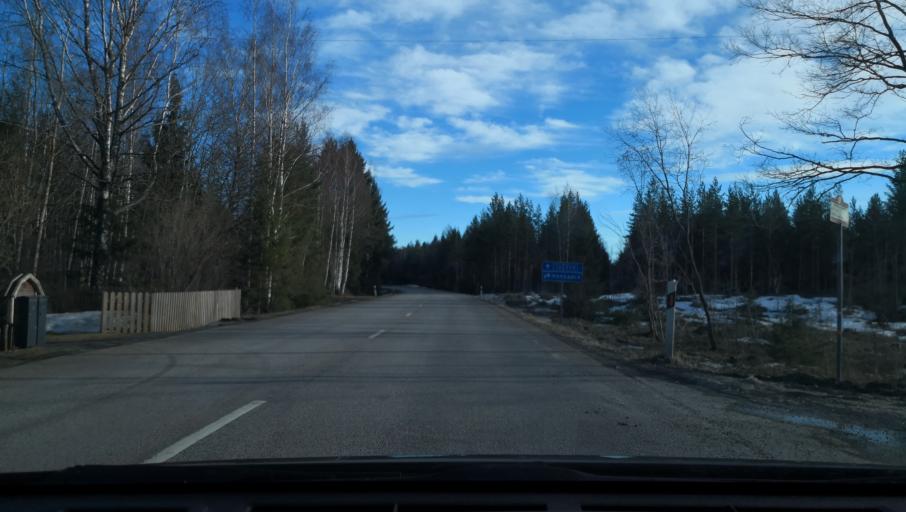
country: SE
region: Uppsala
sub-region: Osthammars Kommun
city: Osterbybruk
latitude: 60.1748
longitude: 17.9211
